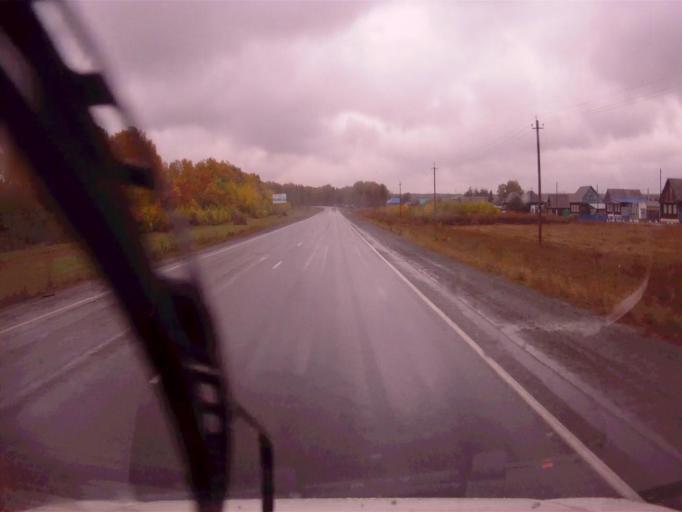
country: RU
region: Chelyabinsk
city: Argayash
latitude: 55.4078
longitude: 61.0550
